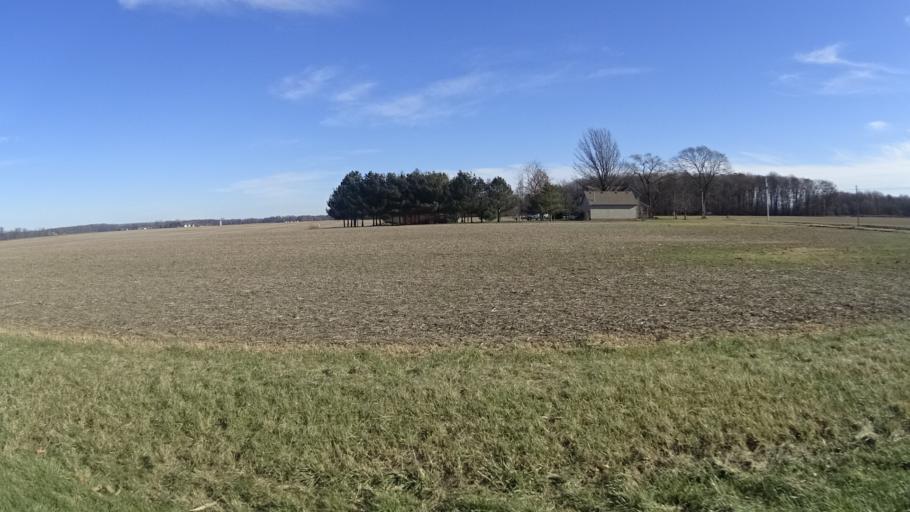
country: US
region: Ohio
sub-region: Lorain County
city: Camden
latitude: 41.2879
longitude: -82.3162
